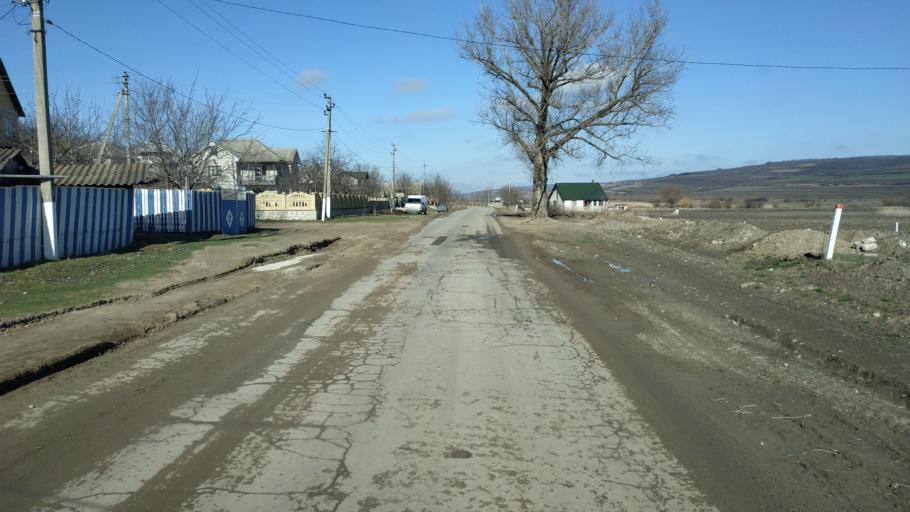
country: MD
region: Hincesti
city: Hincesti
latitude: 46.9359
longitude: 28.6385
